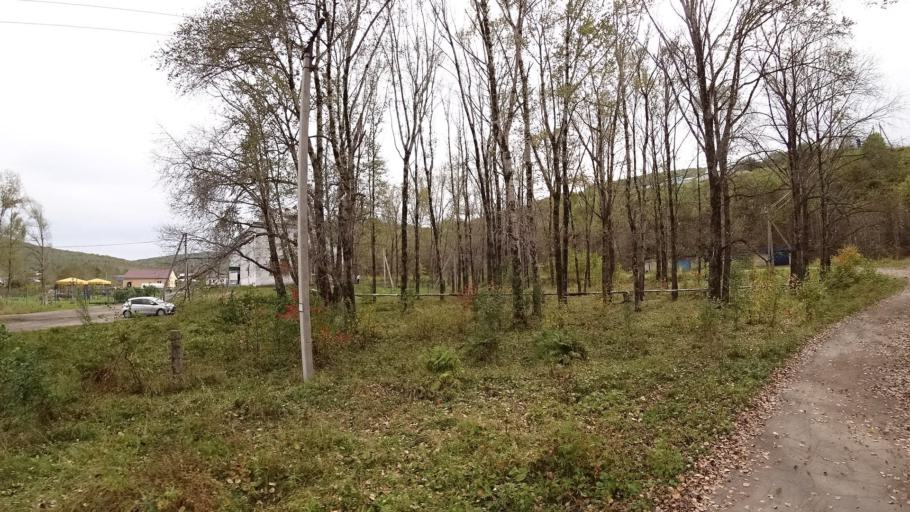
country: RU
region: Jewish Autonomous Oblast
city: Khingansk
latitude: 49.1249
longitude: 131.1980
